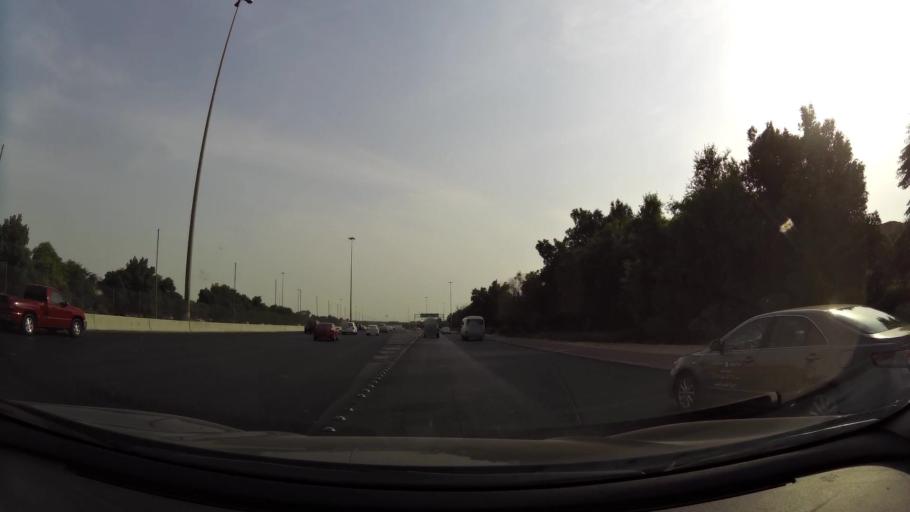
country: KW
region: Al Farwaniyah
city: Janub as Surrah
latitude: 29.2725
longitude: 47.9867
